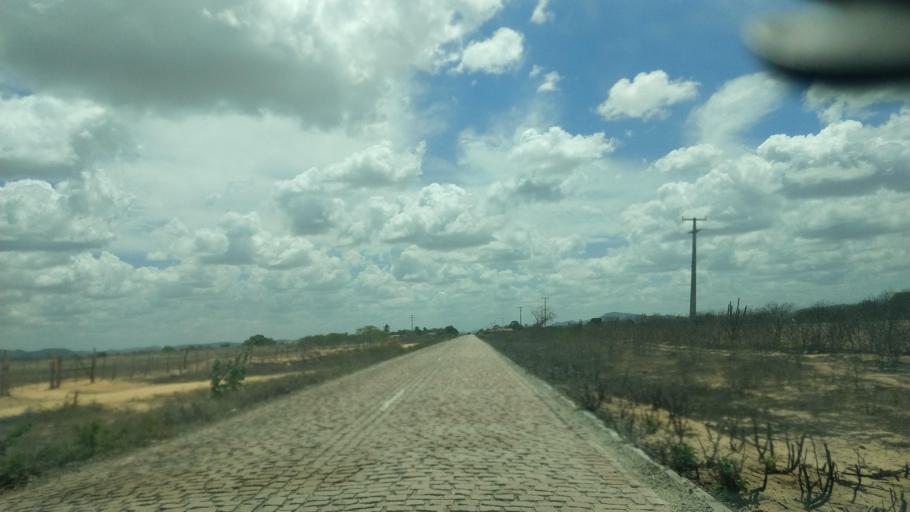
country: BR
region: Rio Grande do Norte
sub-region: Sao Paulo Do Potengi
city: Sao Paulo do Potengi
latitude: -5.9752
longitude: -35.8554
